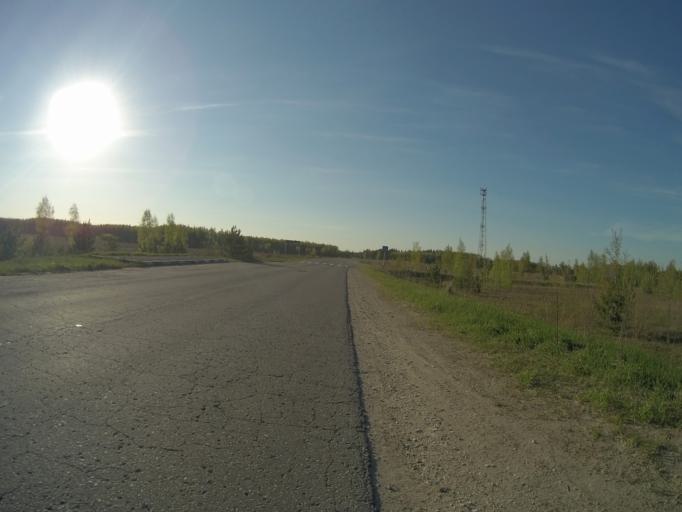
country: RU
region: Vladimir
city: Sudogda
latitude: 56.0979
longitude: 40.7843
